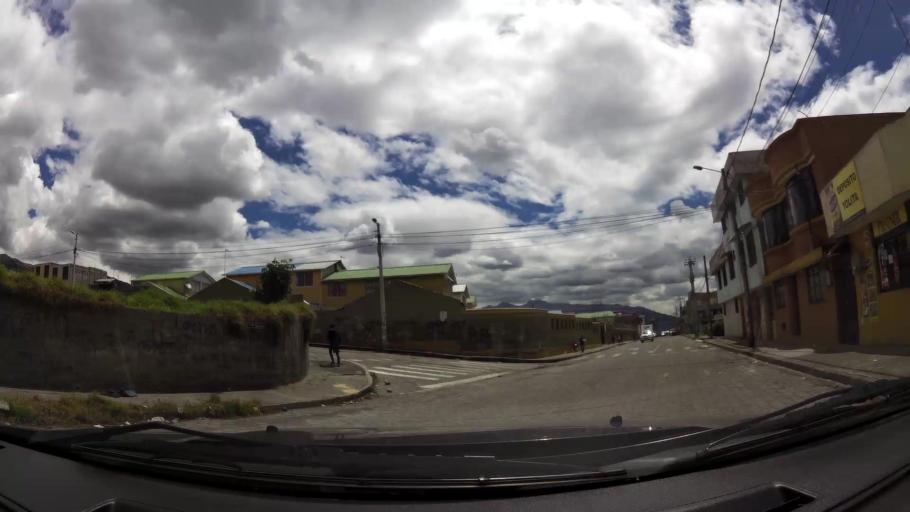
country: EC
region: Pichincha
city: Sangolqui
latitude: -0.3398
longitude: -78.5457
